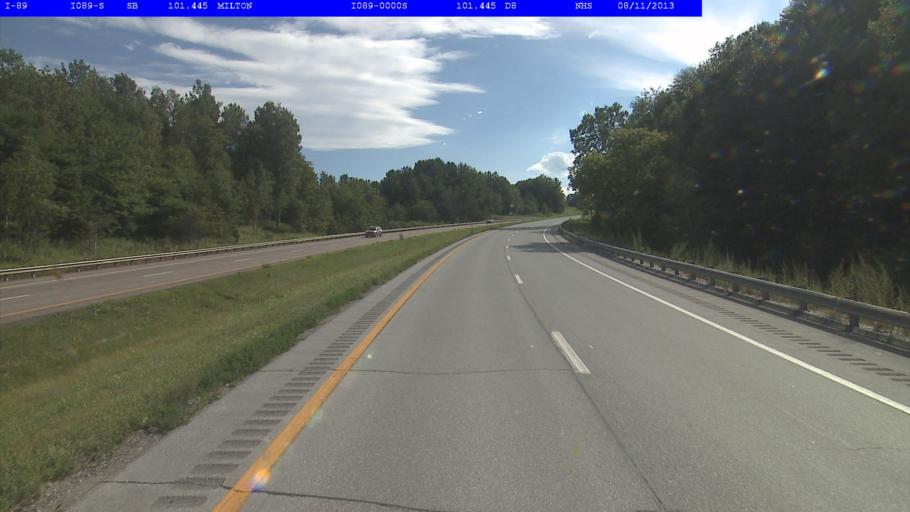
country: US
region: Vermont
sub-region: Chittenden County
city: Milton
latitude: 44.6341
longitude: -73.1418
